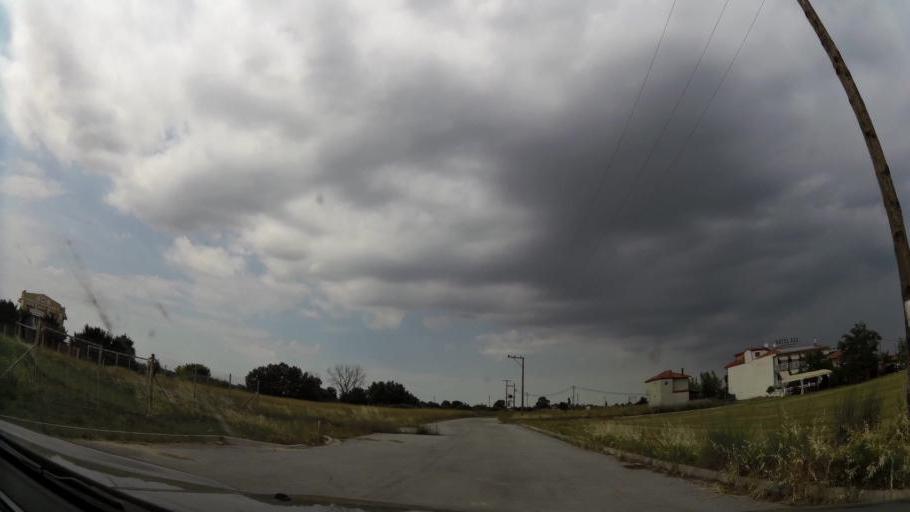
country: GR
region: Central Macedonia
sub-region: Nomos Pierias
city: Paralia
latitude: 40.2770
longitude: 22.5946
